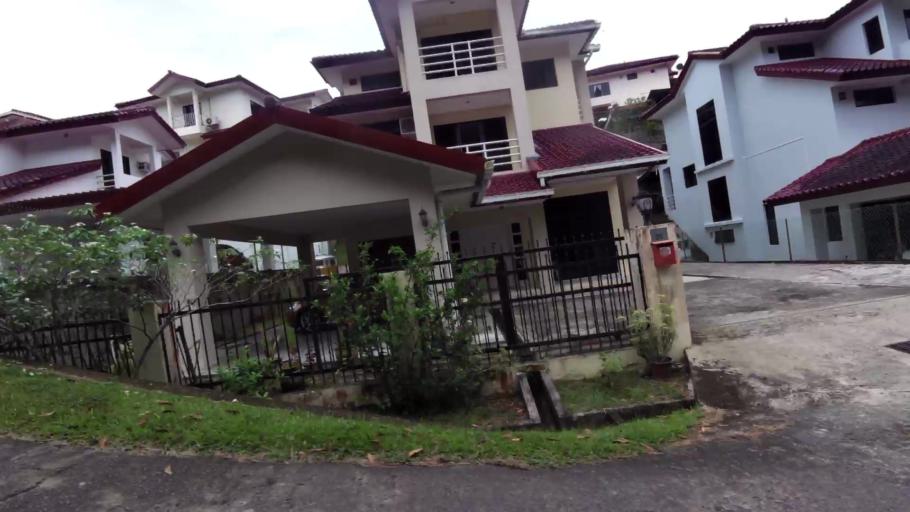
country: BN
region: Brunei and Muara
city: Bandar Seri Begawan
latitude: 4.8881
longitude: 114.9245
